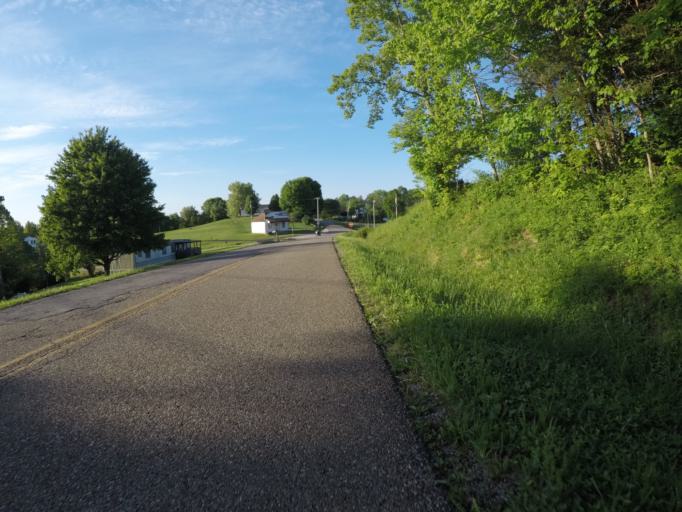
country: US
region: West Virginia
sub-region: Cabell County
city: Huntington
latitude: 38.5530
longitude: -82.4268
